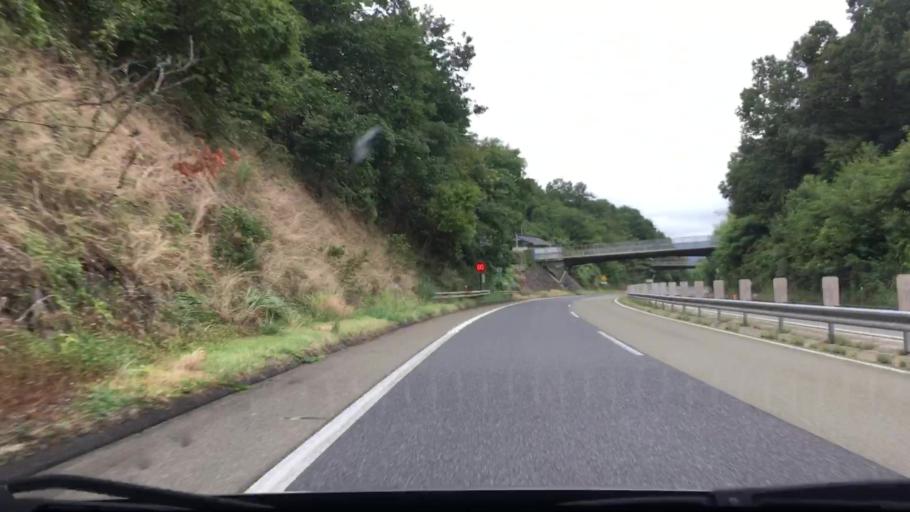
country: JP
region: Hiroshima
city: Shobara
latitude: 34.8290
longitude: 133.0490
